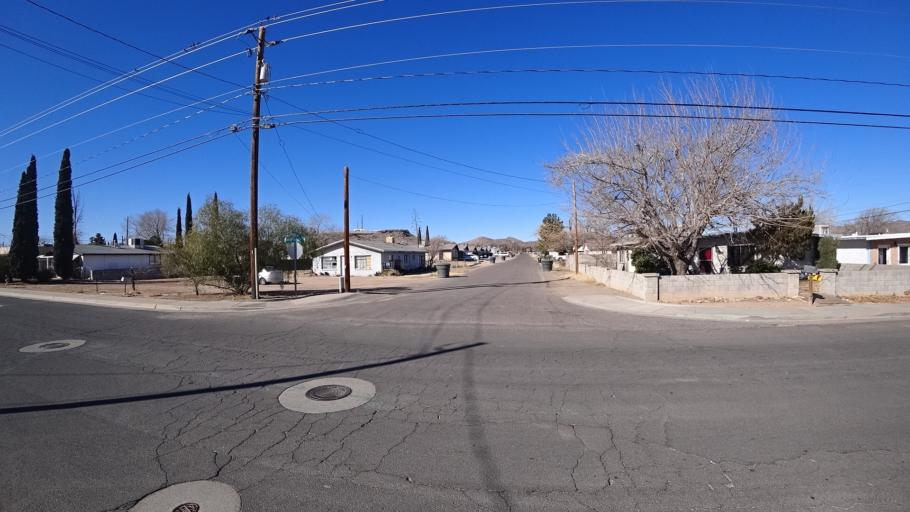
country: US
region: Arizona
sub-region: Mohave County
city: Kingman
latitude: 35.2024
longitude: -114.0291
